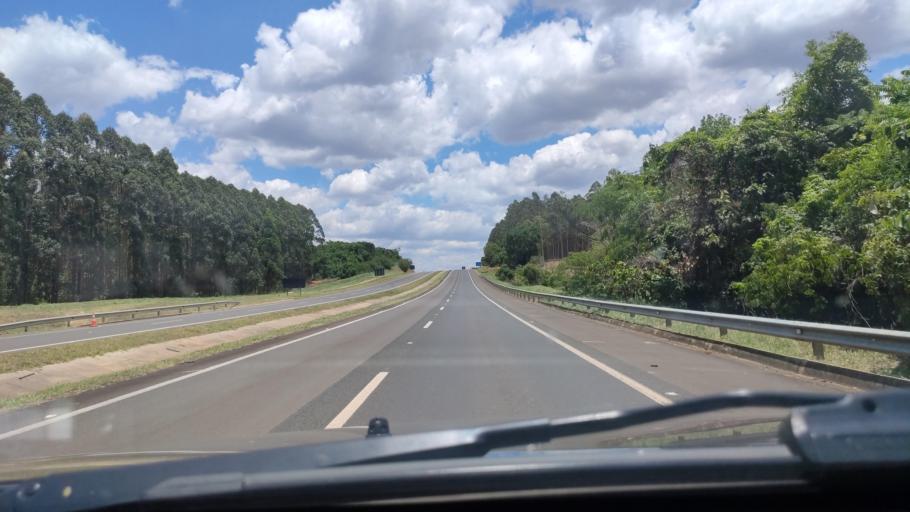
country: BR
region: Sao Paulo
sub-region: Duartina
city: Duartina
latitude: -22.4931
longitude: -49.2566
